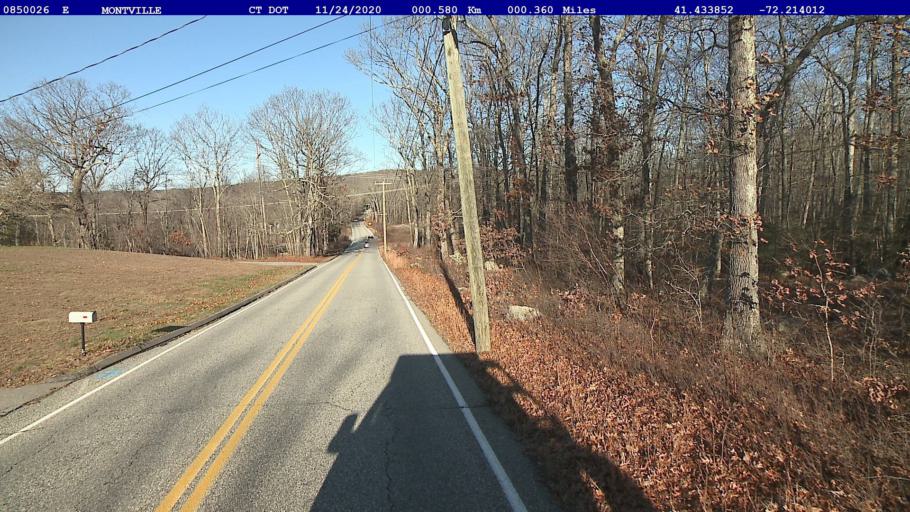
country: US
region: Connecticut
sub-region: New London County
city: Montville Center
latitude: 41.4339
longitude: -72.2140
